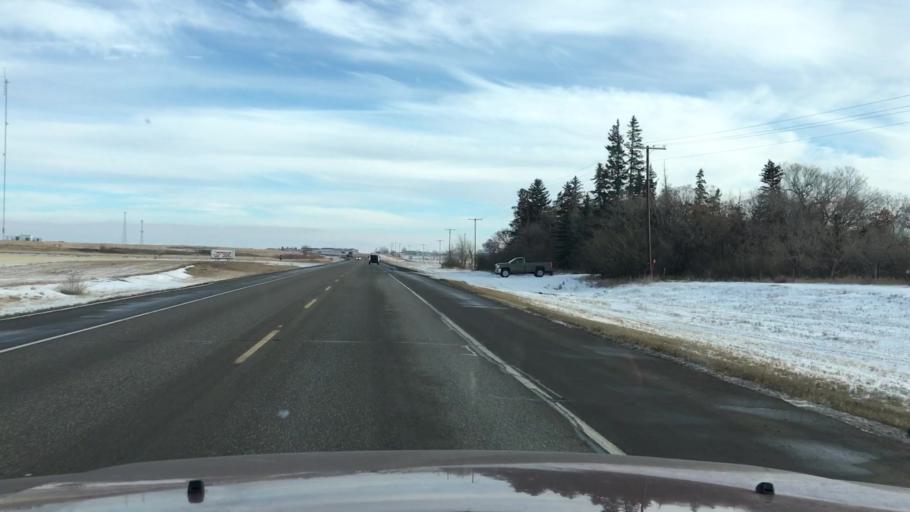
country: CA
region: Saskatchewan
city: Pilot Butte
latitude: 50.4844
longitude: -104.4496
